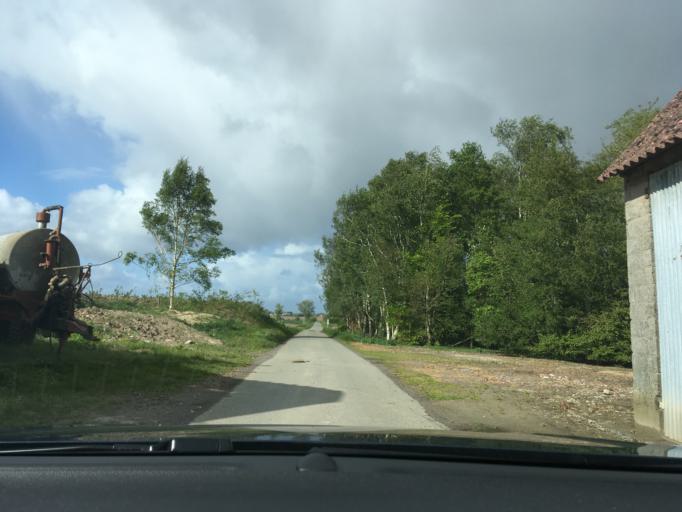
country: BE
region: Flanders
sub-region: Provincie West-Vlaanderen
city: Hooglede
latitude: 51.0075
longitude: 3.0649
